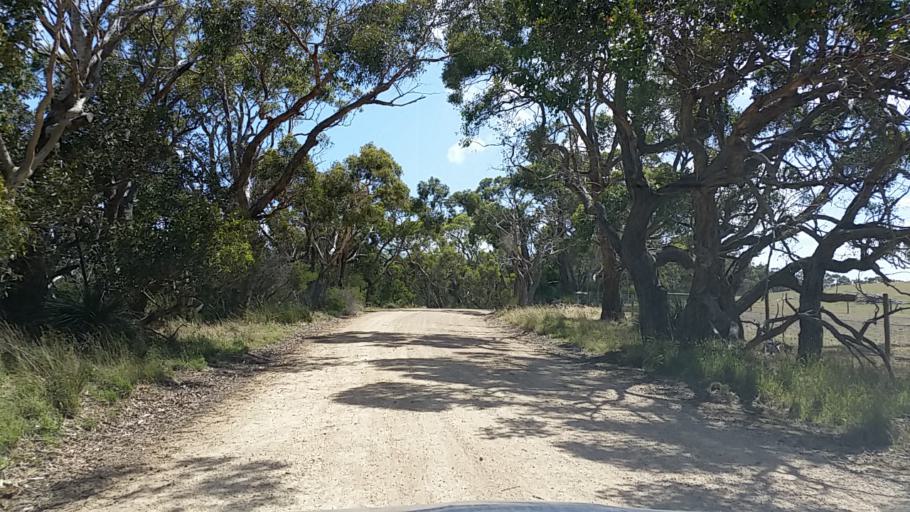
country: AU
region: South Australia
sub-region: Alexandrina
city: Port Elliot
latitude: -35.4507
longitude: 138.6567
